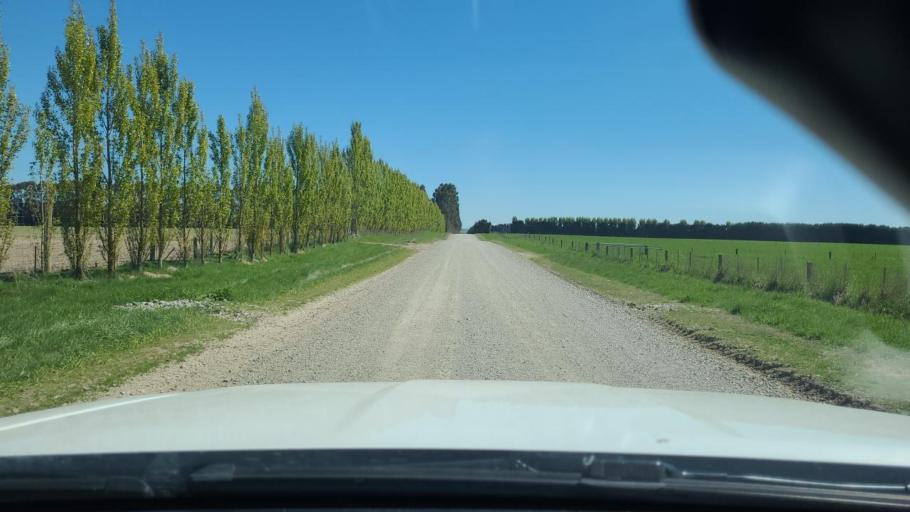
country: NZ
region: Southland
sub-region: Gore District
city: Gore
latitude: -45.7914
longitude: 168.6898
